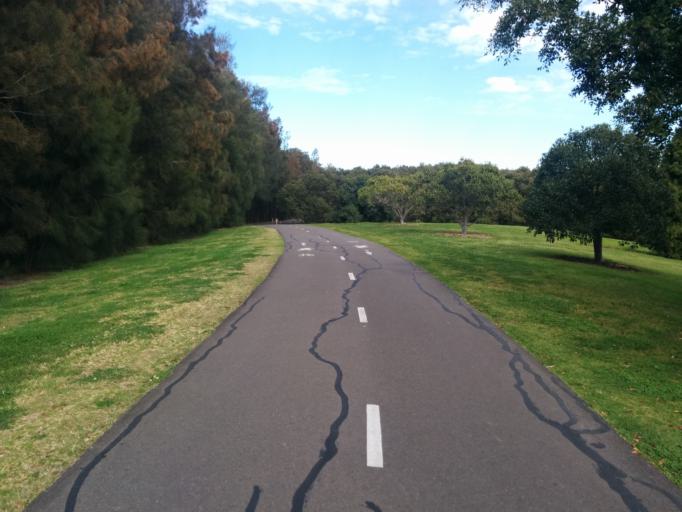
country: AU
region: New South Wales
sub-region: Canada Bay
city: Concord West
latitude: -33.8387
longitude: 151.0828
